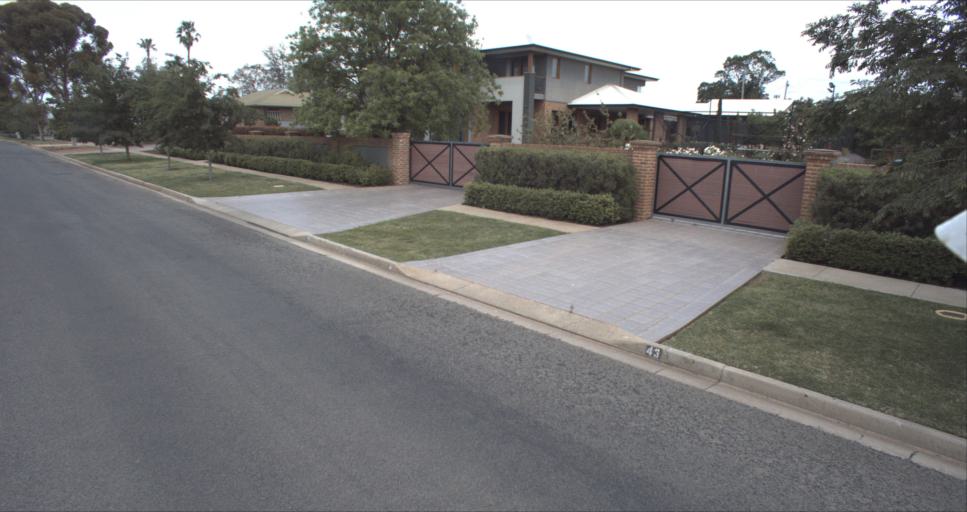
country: AU
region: New South Wales
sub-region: Leeton
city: Leeton
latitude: -34.5515
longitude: 146.4117
